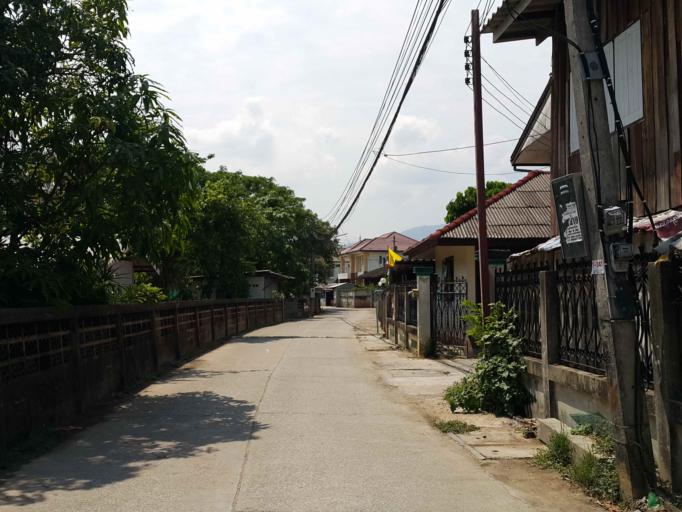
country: TH
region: Chiang Mai
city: Chiang Mai
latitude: 18.7453
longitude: 98.9585
